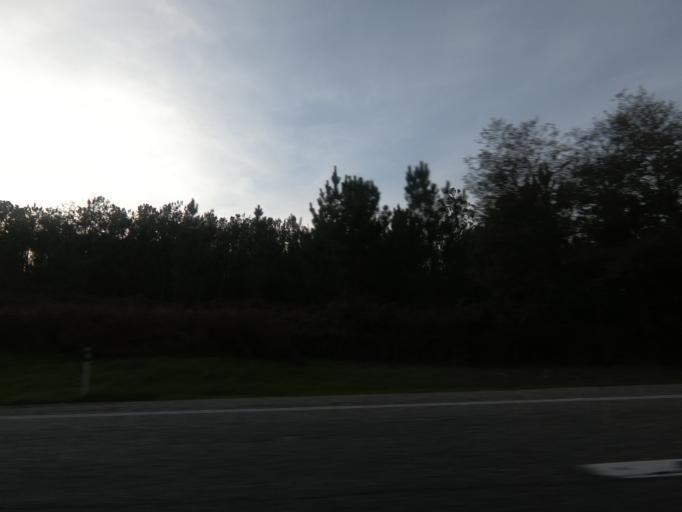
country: PT
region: Leiria
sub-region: Leiria
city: Caranguejeira
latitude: 39.7539
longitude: -8.7492
